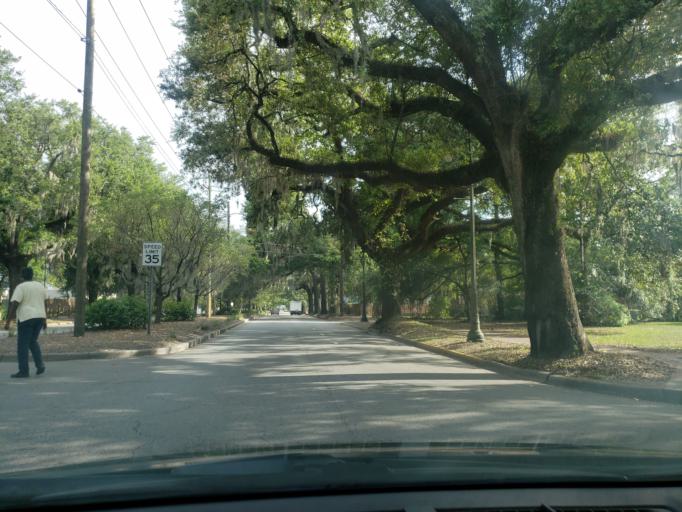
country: US
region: Georgia
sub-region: Chatham County
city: Savannah
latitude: 32.0533
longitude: -81.1074
